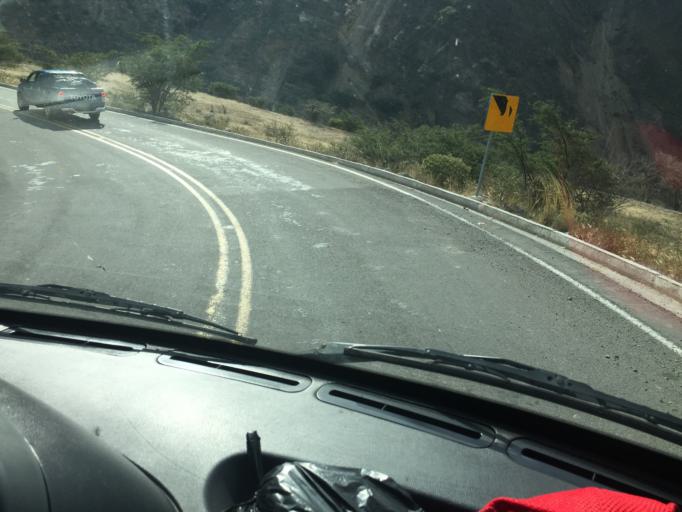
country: EC
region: Carchi
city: El Angel
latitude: 0.6048
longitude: -78.1352
